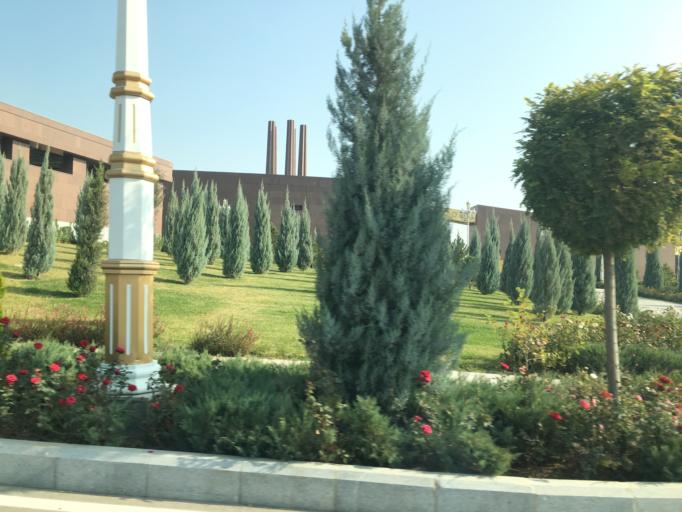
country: TM
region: Ahal
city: Ashgabat
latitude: 37.9361
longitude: 58.3115
